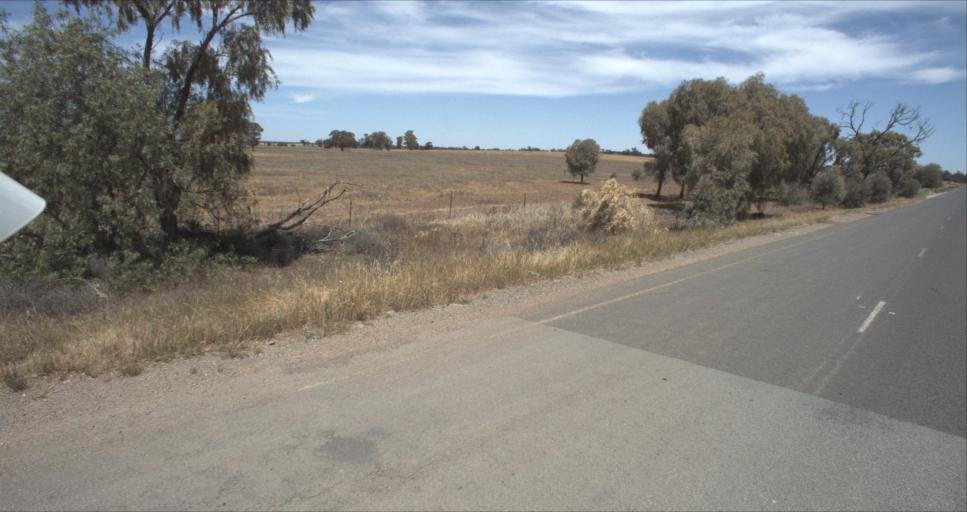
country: AU
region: New South Wales
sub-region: Leeton
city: Leeton
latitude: -34.6492
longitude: 146.4688
